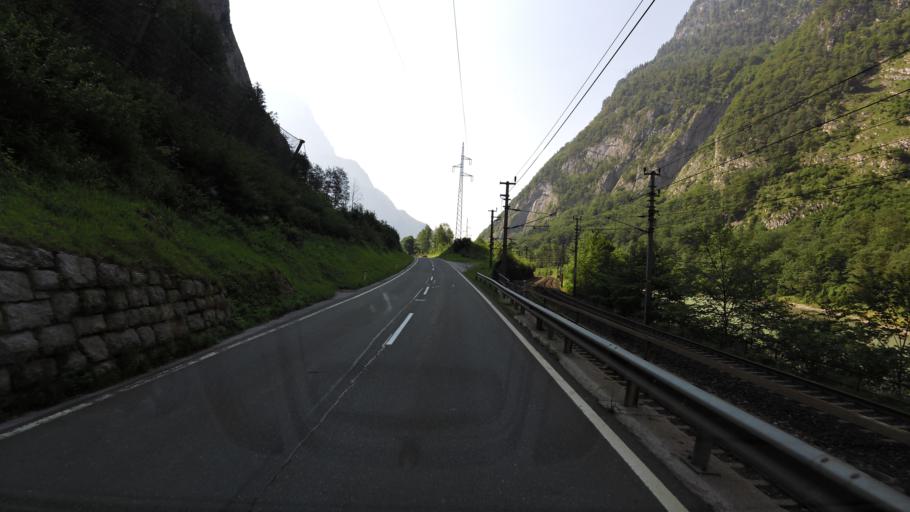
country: AT
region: Salzburg
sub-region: Politischer Bezirk Hallein
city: Golling an der Salzach
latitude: 47.5590
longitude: 13.1662
